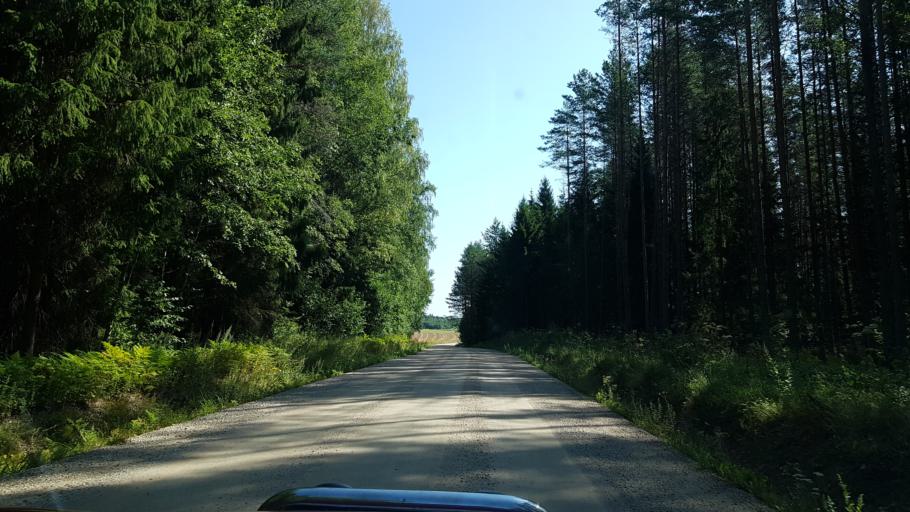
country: EE
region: Vorumaa
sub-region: Voru linn
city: Voru
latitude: 57.7362
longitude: 27.2377
